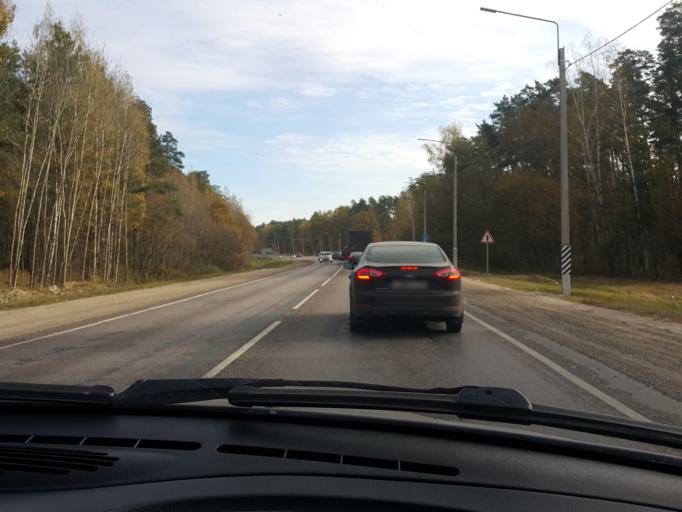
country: RU
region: Tambov
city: Donskoye
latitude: 52.7070
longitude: 41.5416
